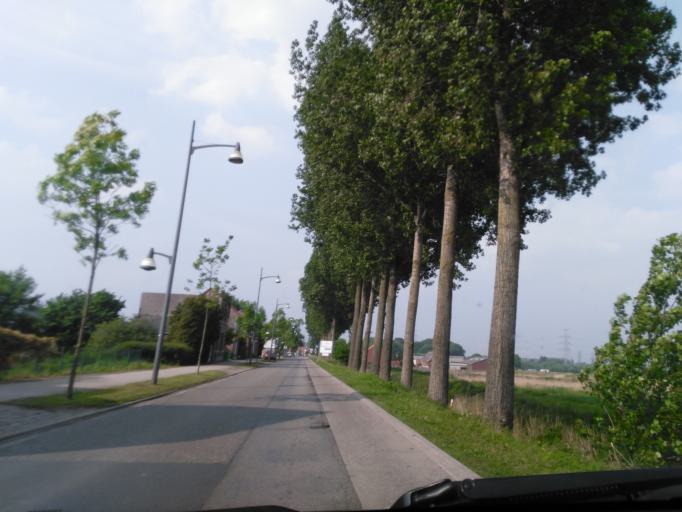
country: BE
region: Flanders
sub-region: Provincie Oost-Vlaanderen
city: Beveren
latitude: 51.2478
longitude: 4.2756
